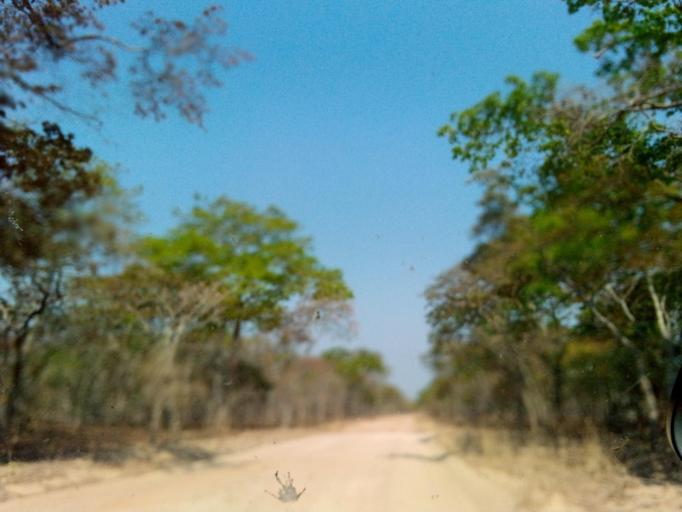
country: ZM
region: Northern
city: Mpika
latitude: -12.2422
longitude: 30.8382
